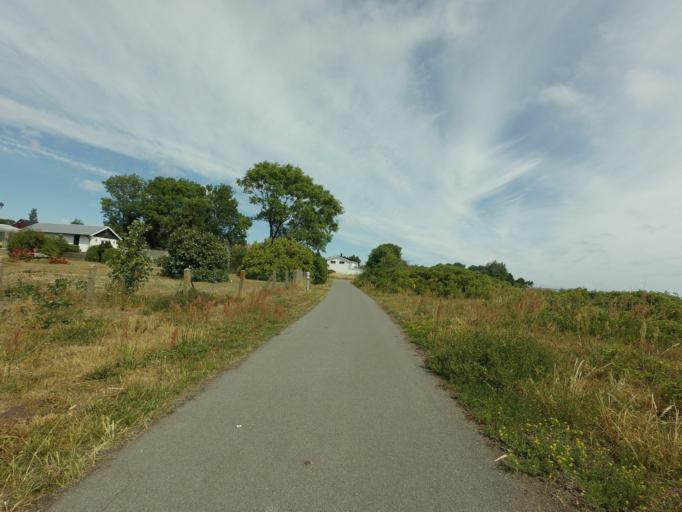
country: SE
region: Skane
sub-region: Simrishamns Kommun
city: Simrishamn
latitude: 55.5243
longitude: 14.3475
